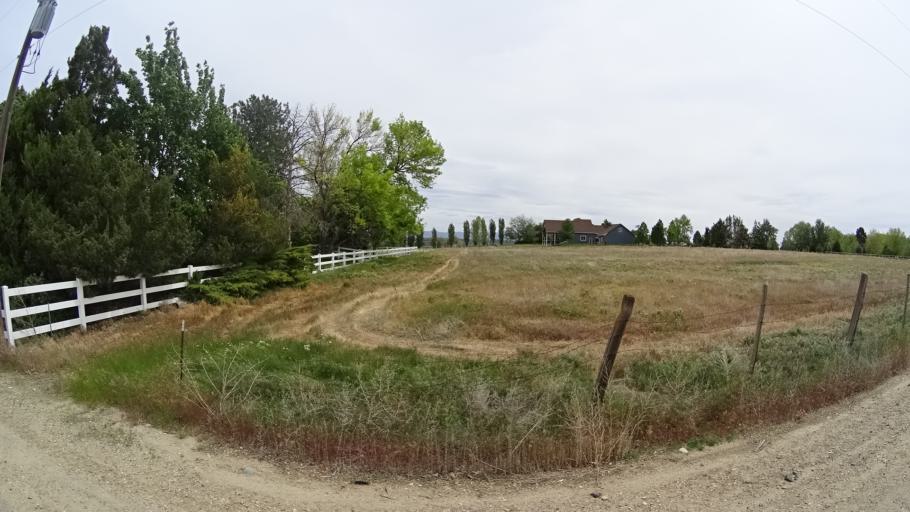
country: US
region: Idaho
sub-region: Ada County
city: Meridian
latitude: 43.5555
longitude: -116.3746
